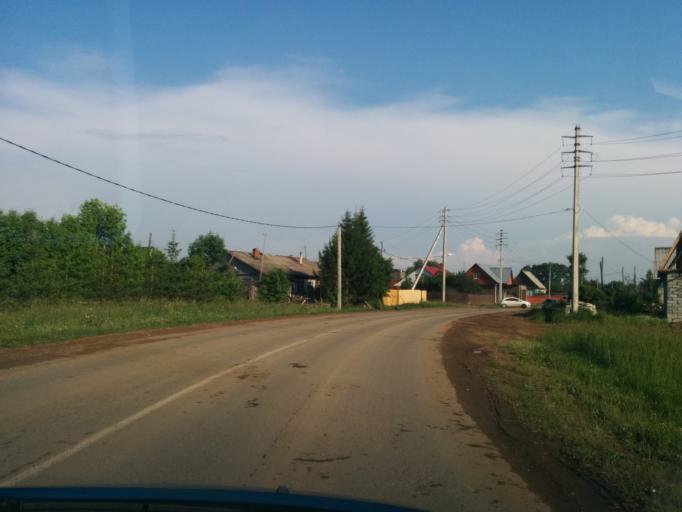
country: RU
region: Perm
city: Polazna
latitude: 58.2371
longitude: 56.2863
